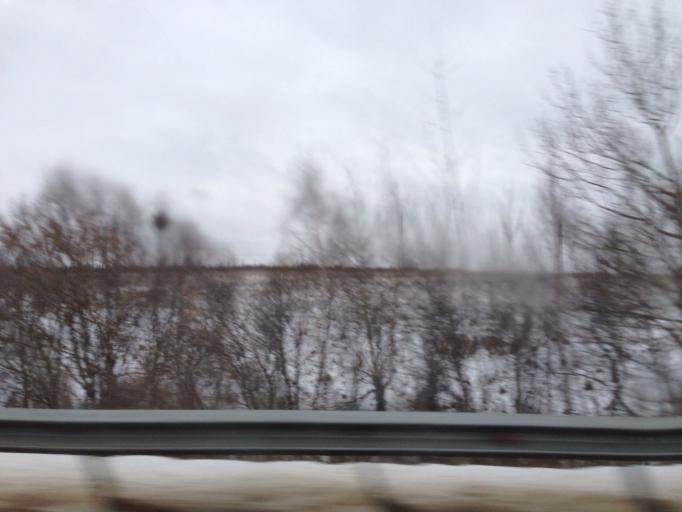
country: RU
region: Tula
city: Kamenetskiy
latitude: 53.9970
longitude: 38.2063
